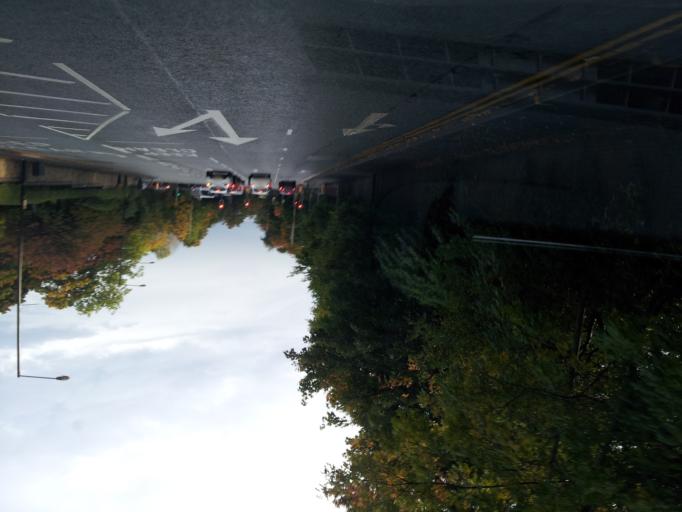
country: GB
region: England
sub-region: Manchester
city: Crumpsall
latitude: 53.5151
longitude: -2.2481
